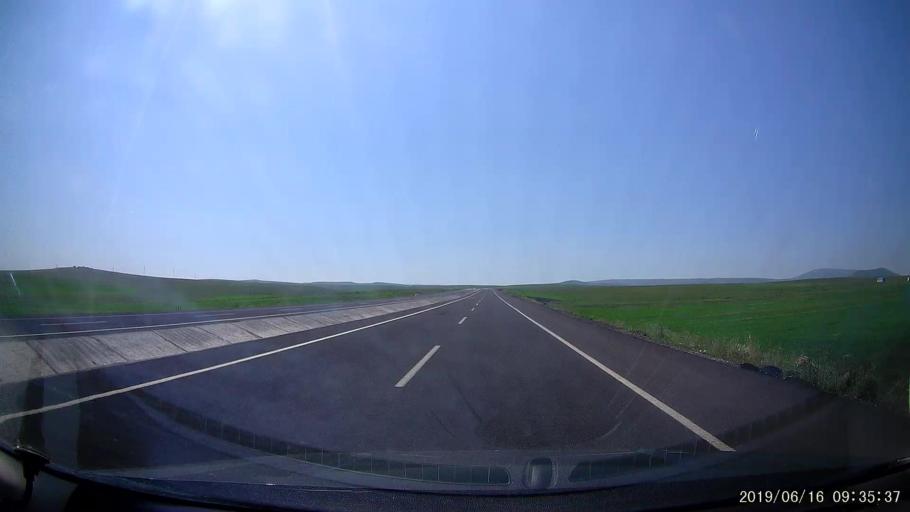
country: TR
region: Kars
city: Kars
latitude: 40.5691
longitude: 43.1590
